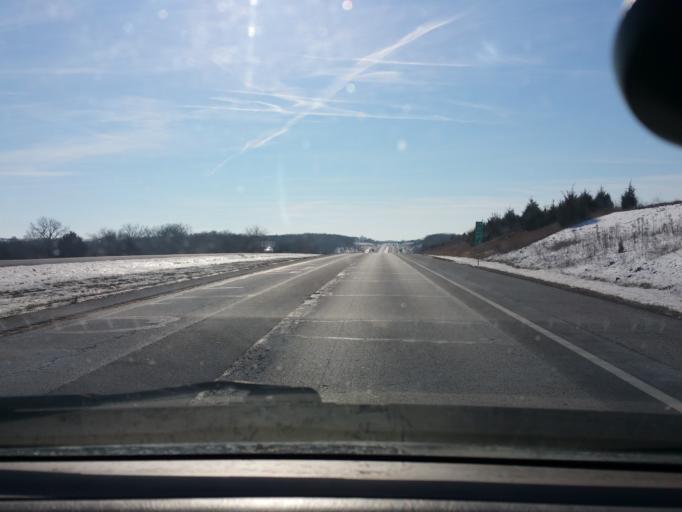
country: US
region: Missouri
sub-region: Harrison County
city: Bethany
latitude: 40.2250
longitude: -94.0131
